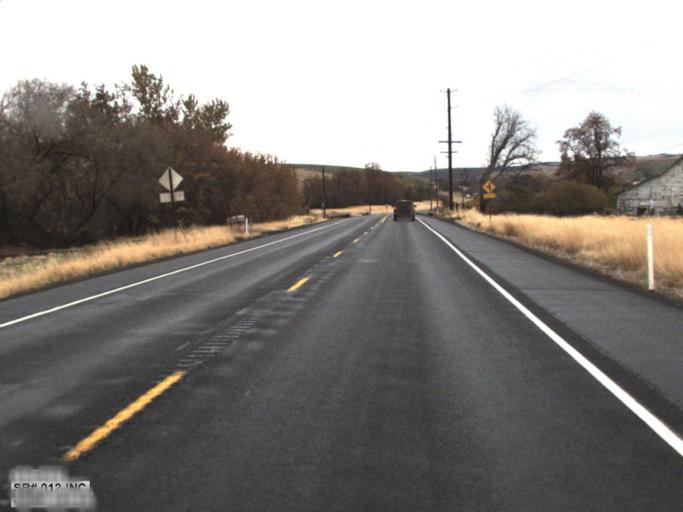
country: US
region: Washington
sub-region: Walla Walla County
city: Walla Walla East
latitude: 46.1178
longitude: -118.2178
